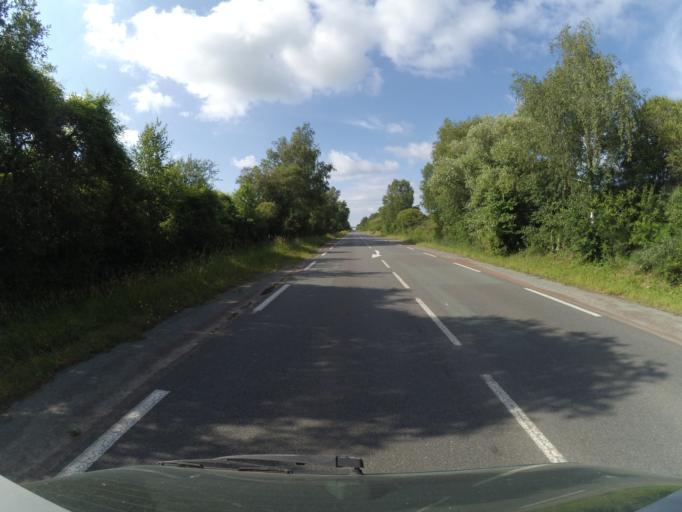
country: FR
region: Poitou-Charentes
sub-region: Departement de la Charente-Maritime
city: Le Gua
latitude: 45.7795
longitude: -0.9362
